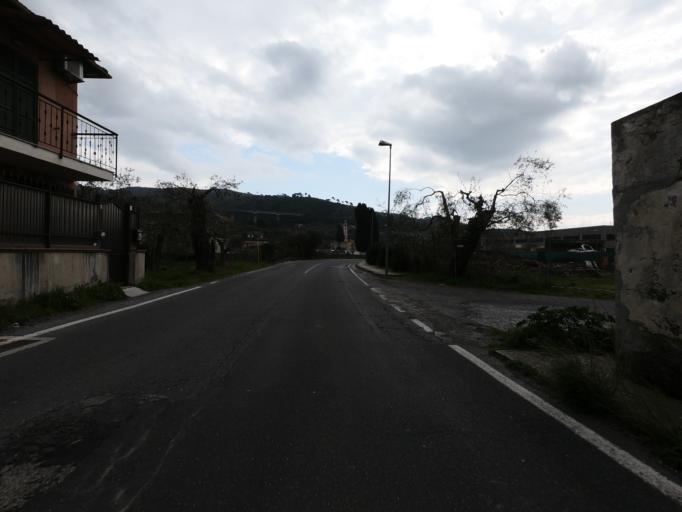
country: IT
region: Liguria
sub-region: Provincia di Savona
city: Laigueglia
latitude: 43.9860
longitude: 8.1283
